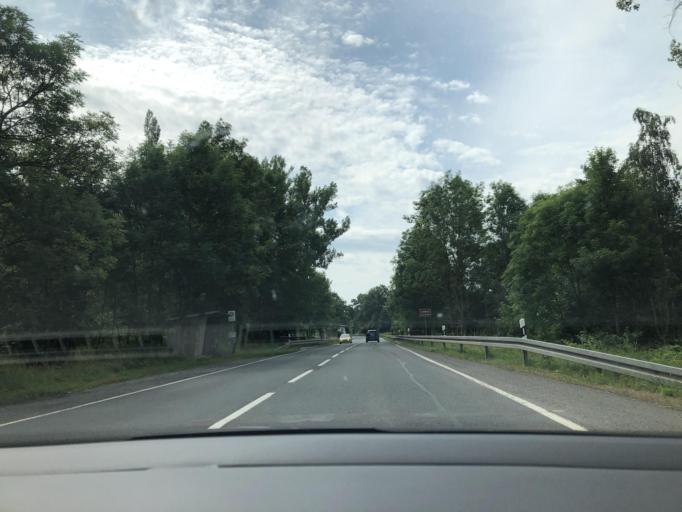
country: DE
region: Saxony-Anhalt
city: Blankenburg
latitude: 51.8226
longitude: 10.9331
